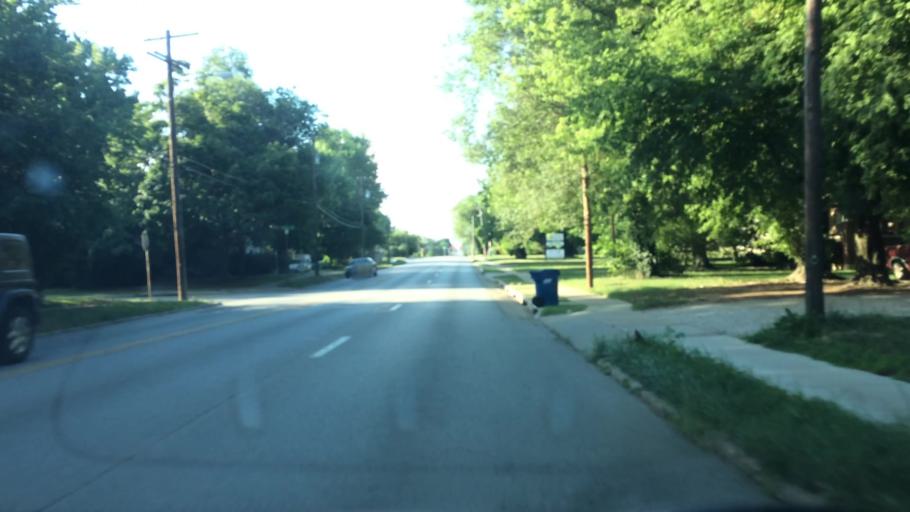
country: US
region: Missouri
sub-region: Greene County
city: Springfield
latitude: 37.1864
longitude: -93.2949
